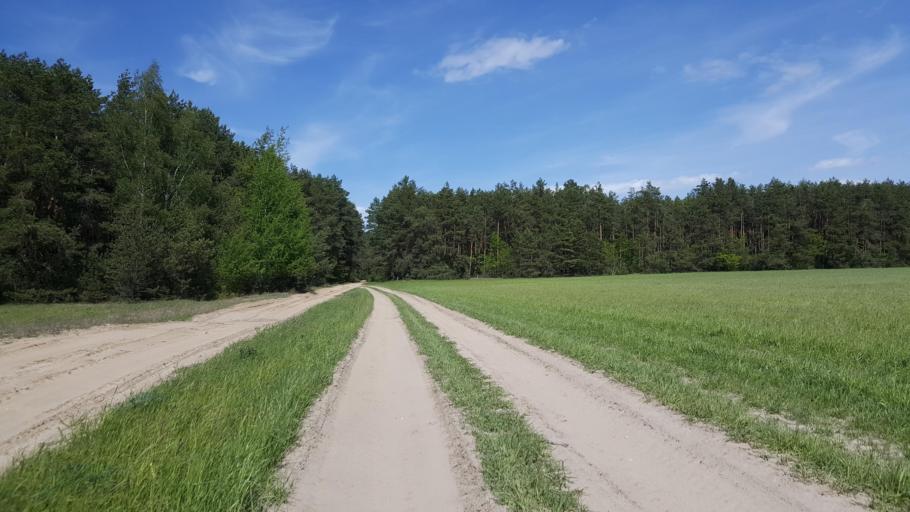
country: BY
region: Brest
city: Zhabinka
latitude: 52.3690
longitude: 24.1628
